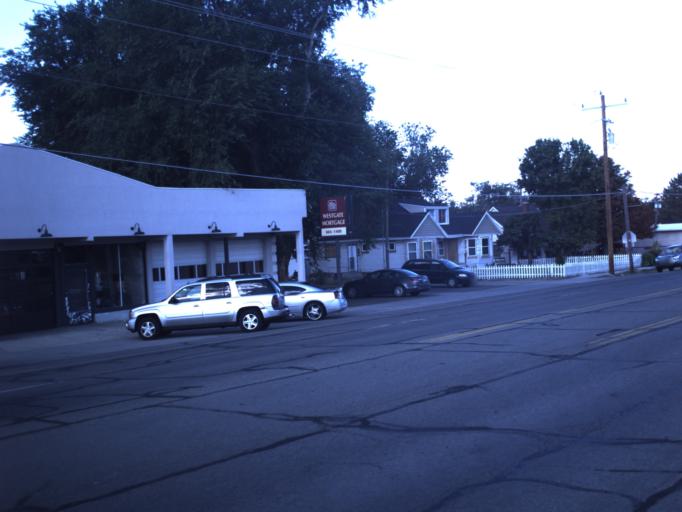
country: US
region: Utah
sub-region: Tooele County
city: Grantsville
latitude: 40.5999
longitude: -112.4671
